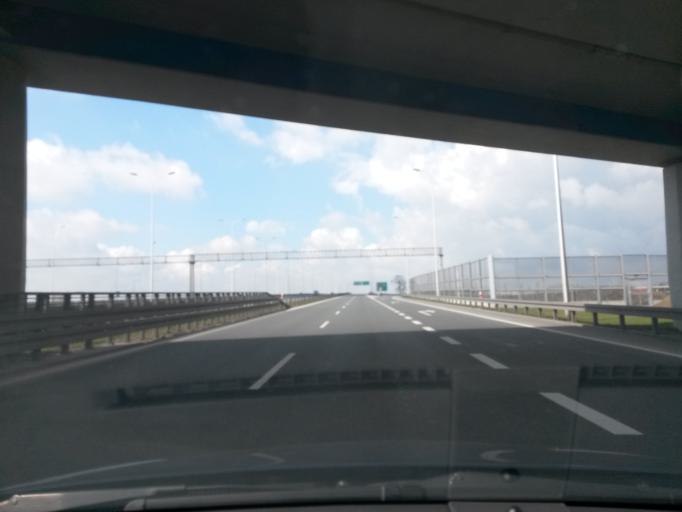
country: PL
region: Masovian Voivodeship
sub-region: Powiat pruszkowski
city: Nowe Grocholice
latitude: 52.1715
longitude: 20.9191
